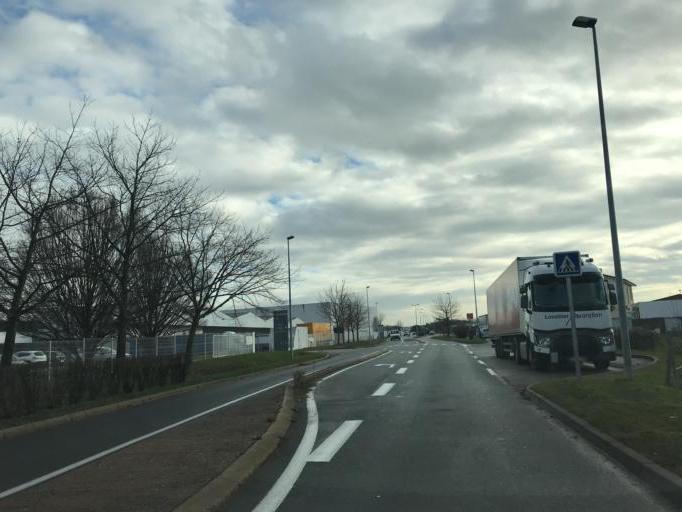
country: FR
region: Rhone-Alpes
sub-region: Departement de l'Ain
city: Reyrieux
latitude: 45.9477
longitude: 4.8092
